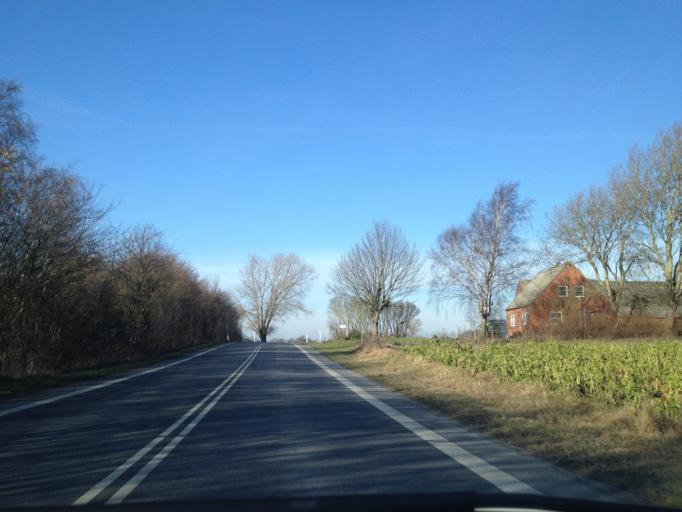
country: DK
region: South Denmark
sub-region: Kerteminde Kommune
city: Kerteminde
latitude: 55.4752
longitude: 10.6663
